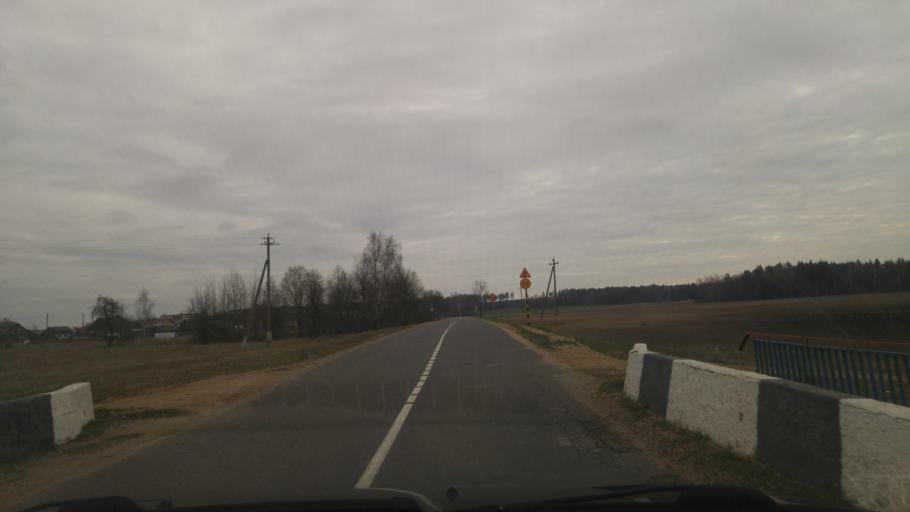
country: BY
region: Minsk
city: Chervyen'
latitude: 53.7288
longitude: 28.2744
